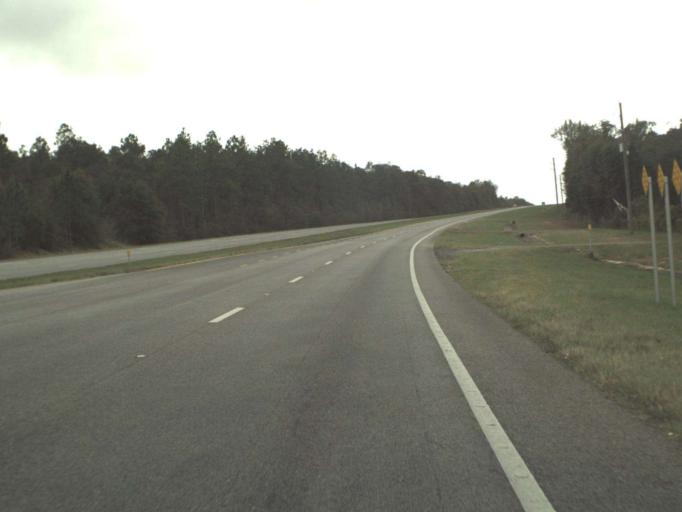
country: US
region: Florida
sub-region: Escambia County
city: Molino
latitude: 30.7620
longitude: -87.3417
